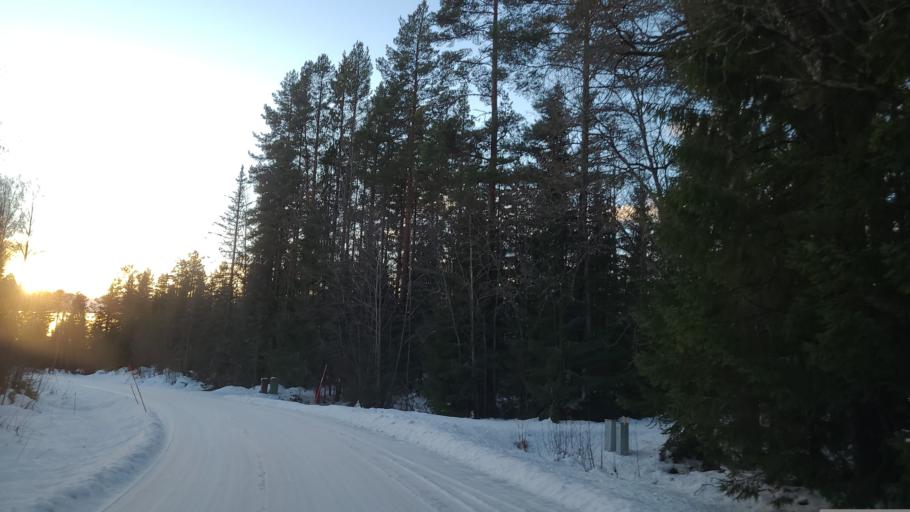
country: SE
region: Gaevleborg
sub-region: Bollnas Kommun
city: Kilafors
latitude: 61.3732
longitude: 16.6796
